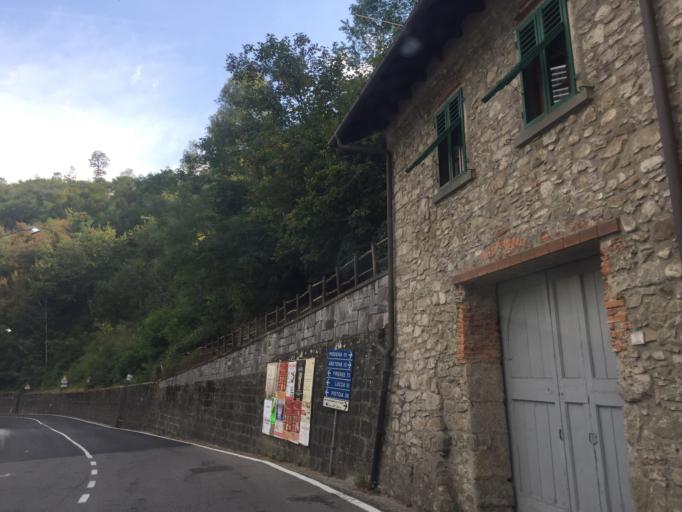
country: IT
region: Tuscany
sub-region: Provincia di Pistoia
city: Cutigliano
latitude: 44.0981
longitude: 10.7510
